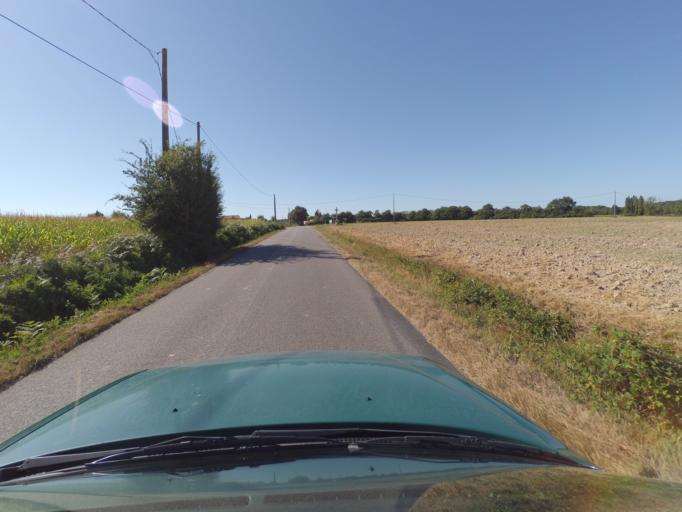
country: FR
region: Pays de la Loire
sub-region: Departement de la Loire-Atlantique
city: Saint-Fiacre-sur-Maine
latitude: 47.1113
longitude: -1.4334
